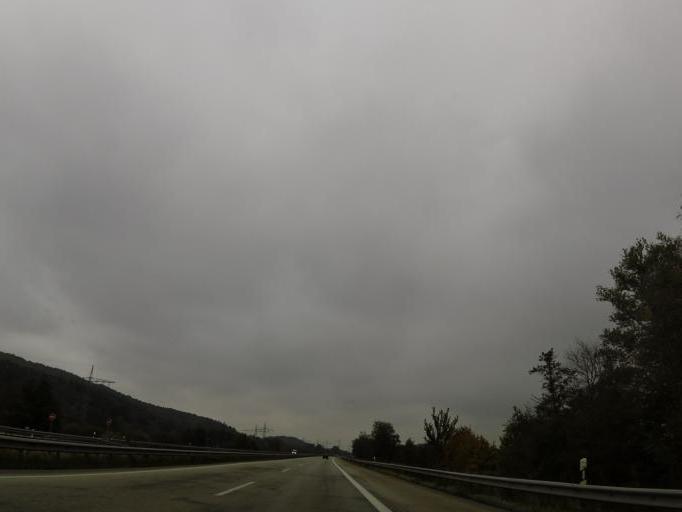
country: DE
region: Rheinland-Pfalz
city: Bruchmuhlbach-Miesau
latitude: 49.3811
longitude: 7.4207
